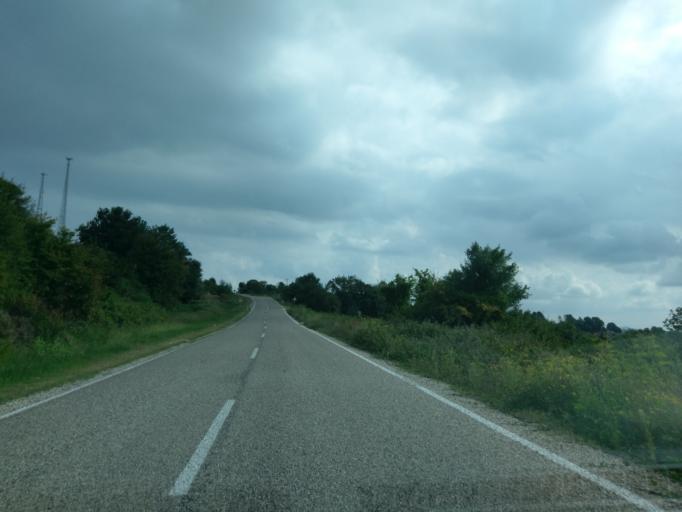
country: TR
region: Sinop
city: Erfelek
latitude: 41.9762
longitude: 34.8703
